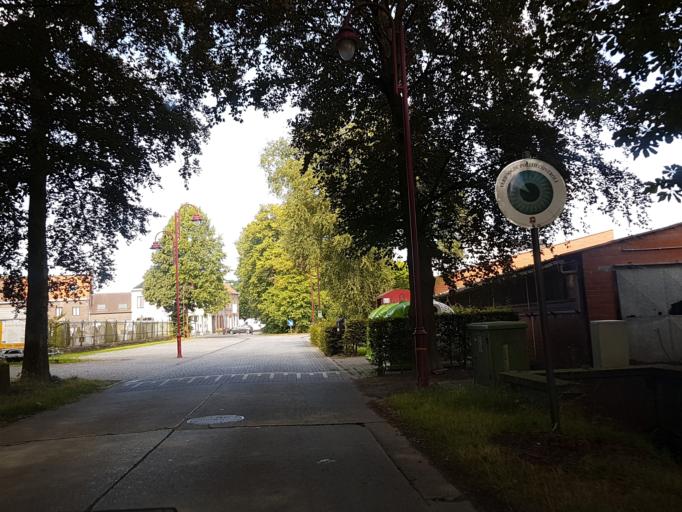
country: BE
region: Flanders
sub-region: Provincie Oost-Vlaanderen
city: Aalter
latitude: 51.0880
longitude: 3.4920
